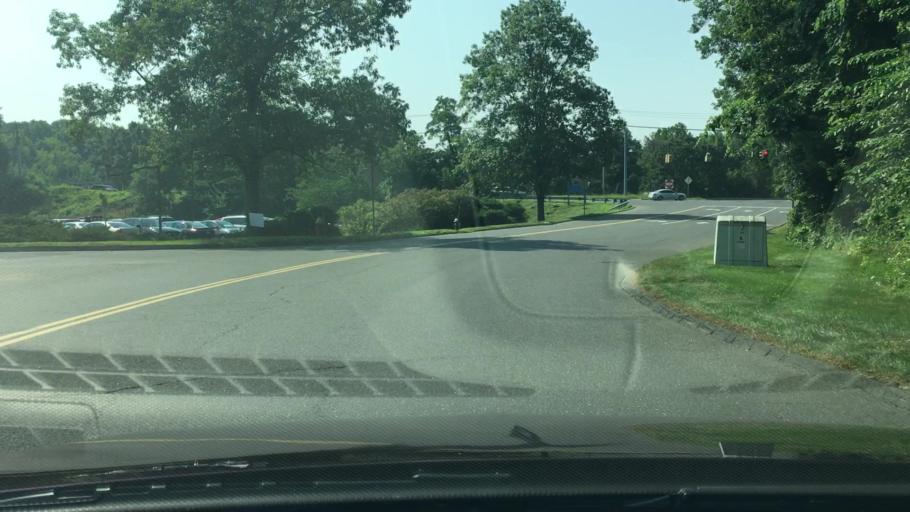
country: US
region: Connecticut
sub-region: Hartford County
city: Farmington
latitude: 41.7083
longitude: -72.8039
